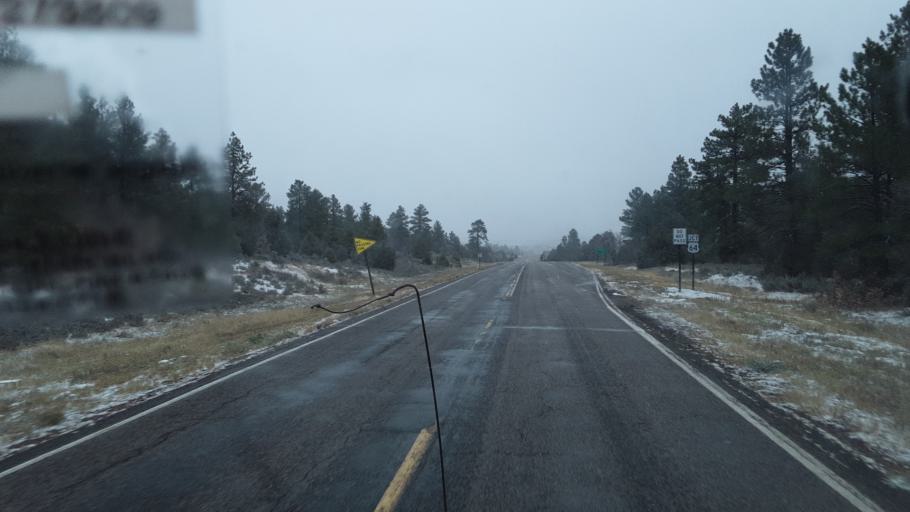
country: US
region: New Mexico
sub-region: Rio Arriba County
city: Tierra Amarilla
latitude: 36.6863
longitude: -106.5580
